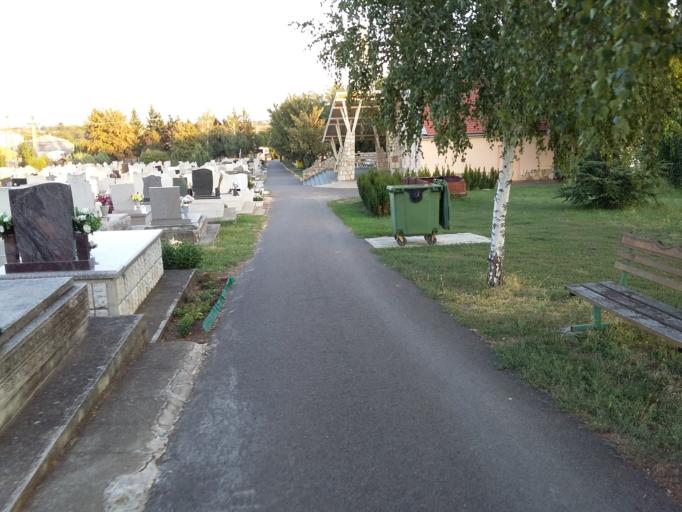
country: HU
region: Borsod-Abauj-Zemplen
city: Bekecs
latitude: 48.1563
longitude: 21.1778
